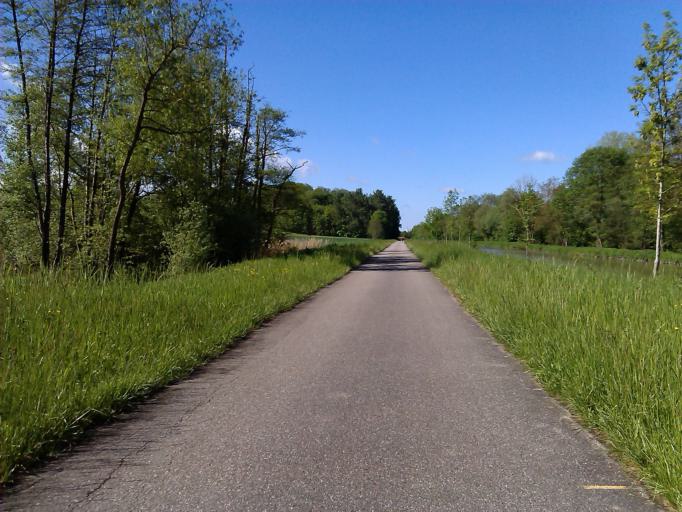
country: FR
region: Alsace
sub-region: Departement du Haut-Rhin
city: Burnhaupt-le-Bas
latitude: 47.6614
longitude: 7.1717
